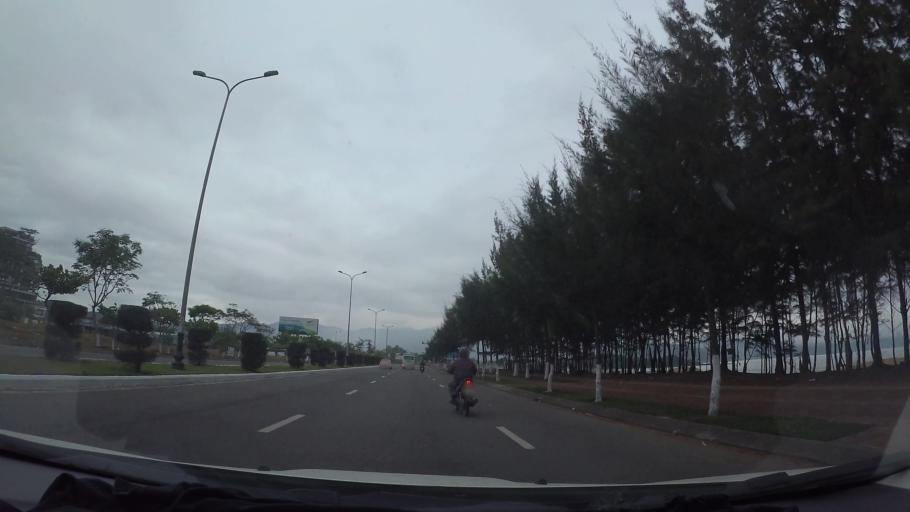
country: VN
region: Da Nang
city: Lien Chieu
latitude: 16.1093
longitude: 108.1333
